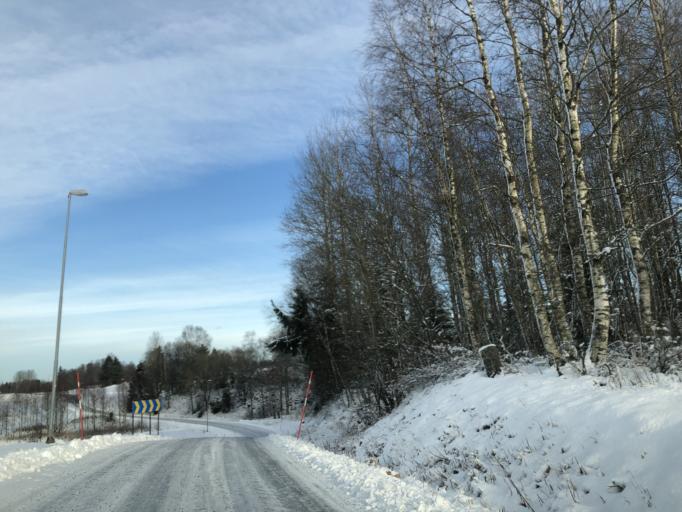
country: SE
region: Vaestra Goetaland
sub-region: Ulricehamns Kommun
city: Ulricehamn
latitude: 57.7913
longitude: 13.5313
